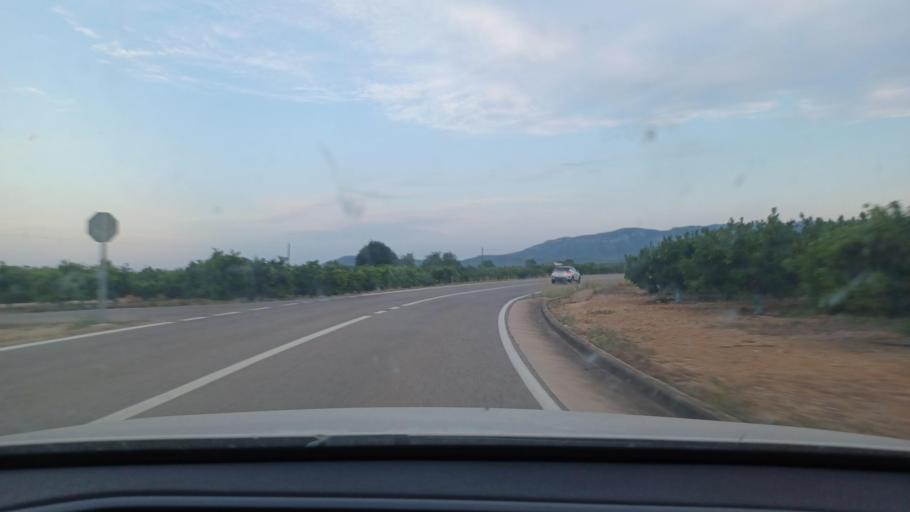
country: ES
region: Catalonia
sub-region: Provincia de Tarragona
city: Santa Barbara
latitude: 40.7191
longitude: 0.4668
